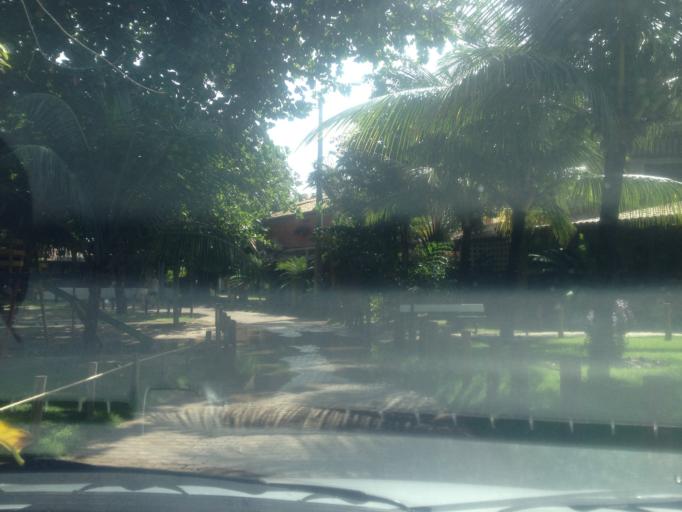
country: BR
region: Bahia
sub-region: Mata De Sao Joao
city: Mata de Sao Joao
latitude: -12.5768
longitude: -38.0032
